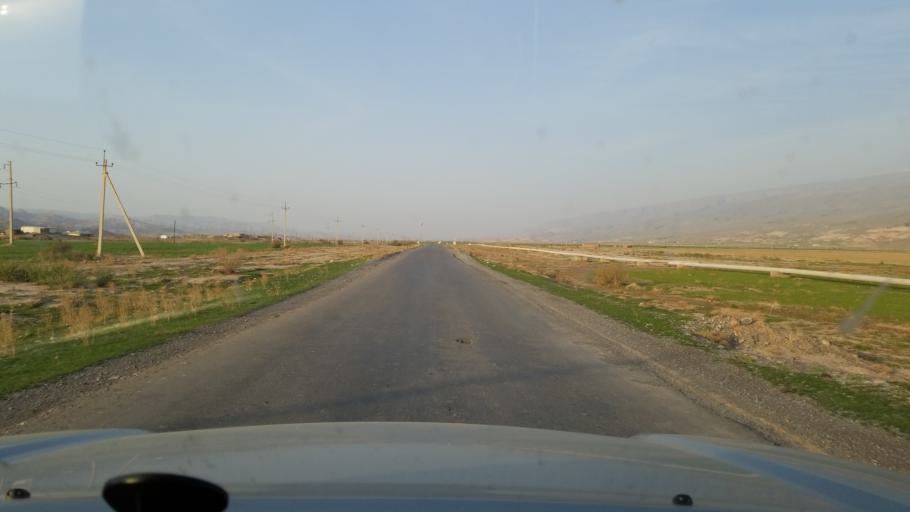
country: TM
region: Lebap
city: Gowurdak
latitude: 37.7563
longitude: 66.3555
